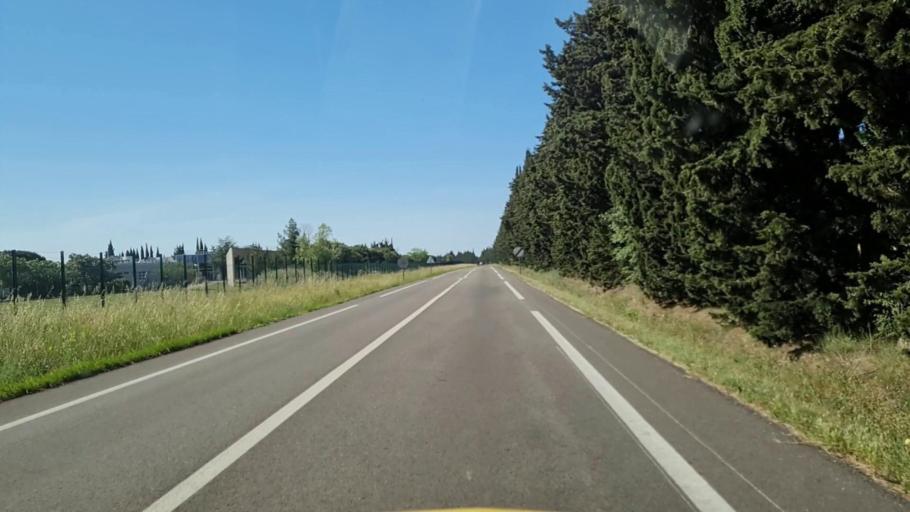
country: FR
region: Languedoc-Roussillon
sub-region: Departement du Gard
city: Garons
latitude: 43.7583
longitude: 4.4060
